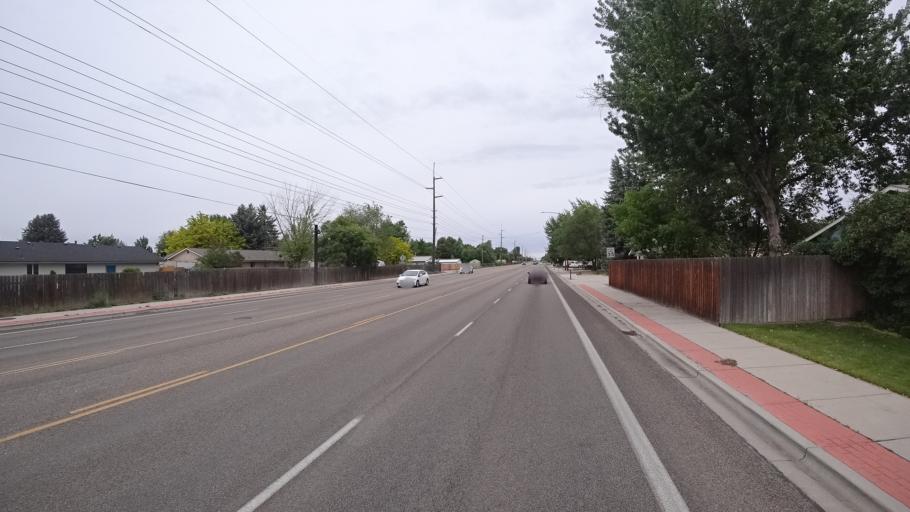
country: US
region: Idaho
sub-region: Ada County
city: Garden City
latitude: 43.6340
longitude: -116.3070
